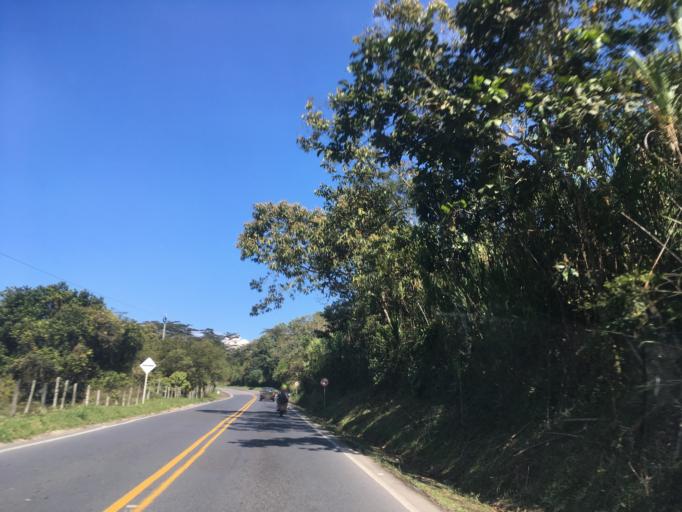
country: CO
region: Santander
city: Suaita
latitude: 6.0823
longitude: -73.3896
